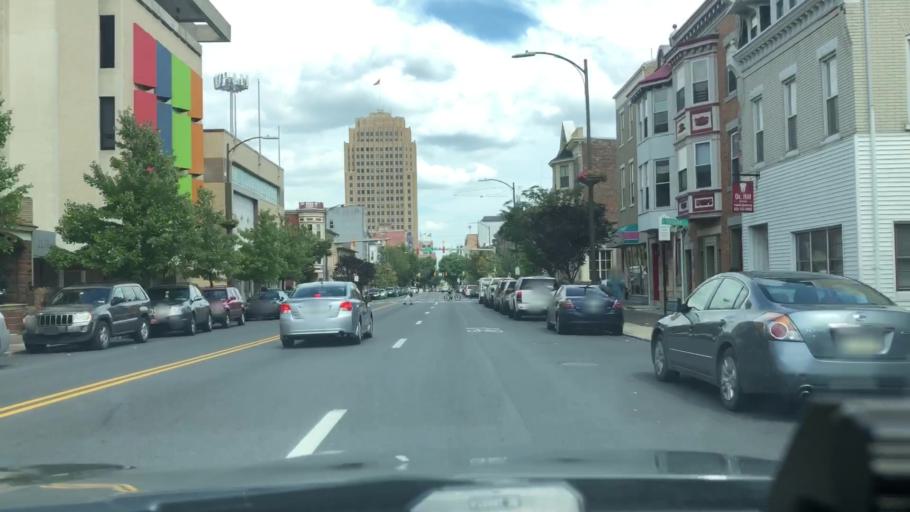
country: US
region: Pennsylvania
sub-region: Lehigh County
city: Allentown
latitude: 40.5997
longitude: -75.4808
